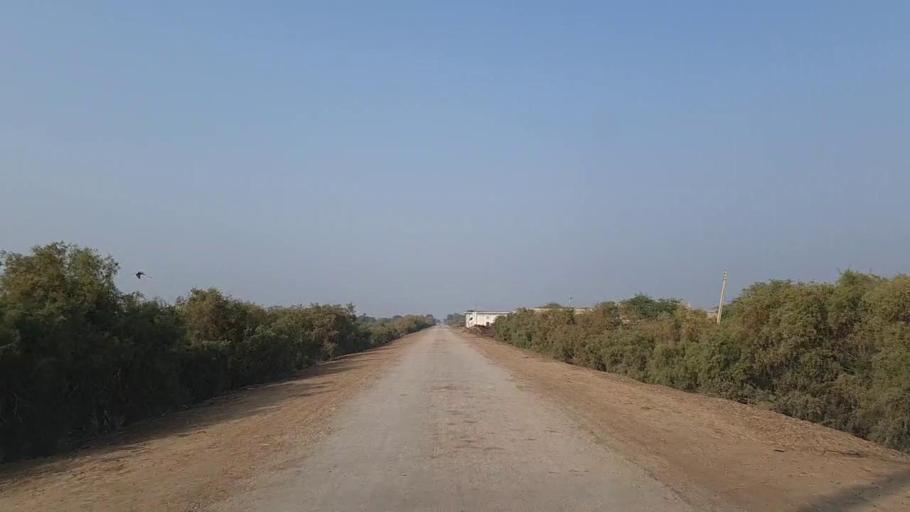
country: PK
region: Sindh
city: Nawabshah
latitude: 26.3370
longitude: 68.4891
